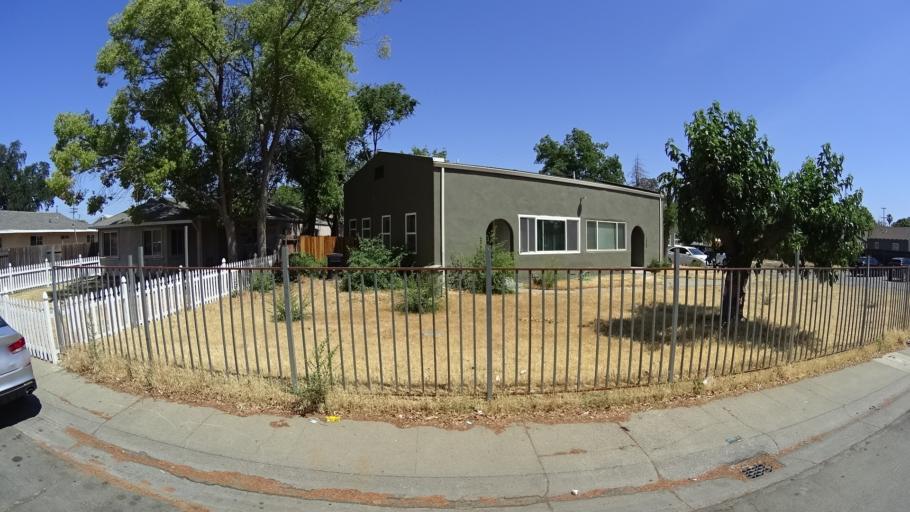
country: US
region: California
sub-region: Sacramento County
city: Parkway
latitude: 38.5182
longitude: -121.4756
